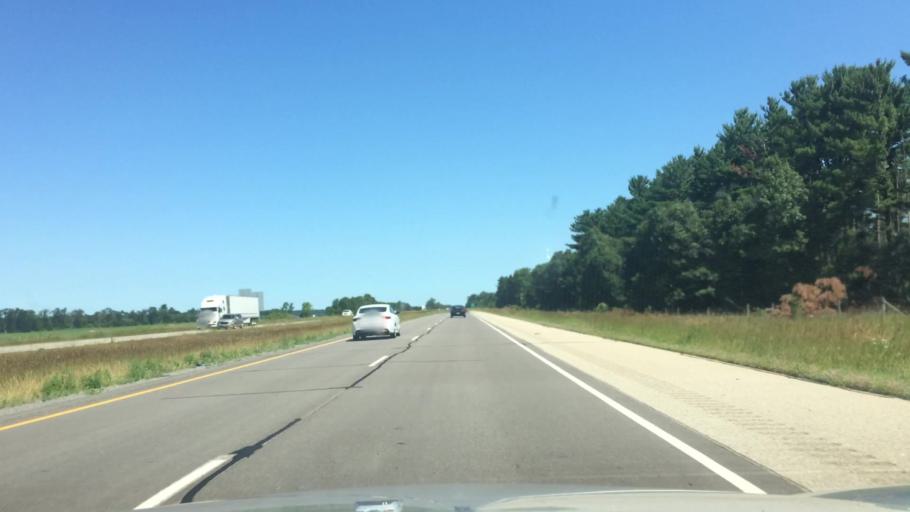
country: US
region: Wisconsin
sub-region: Portage County
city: Plover
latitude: 44.2317
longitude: -89.5241
